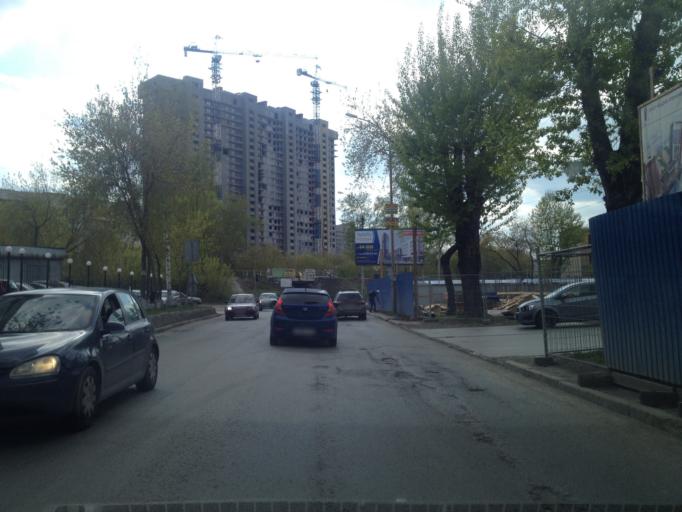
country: RU
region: Sverdlovsk
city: Yekaterinburg
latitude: 56.8557
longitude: 60.5836
